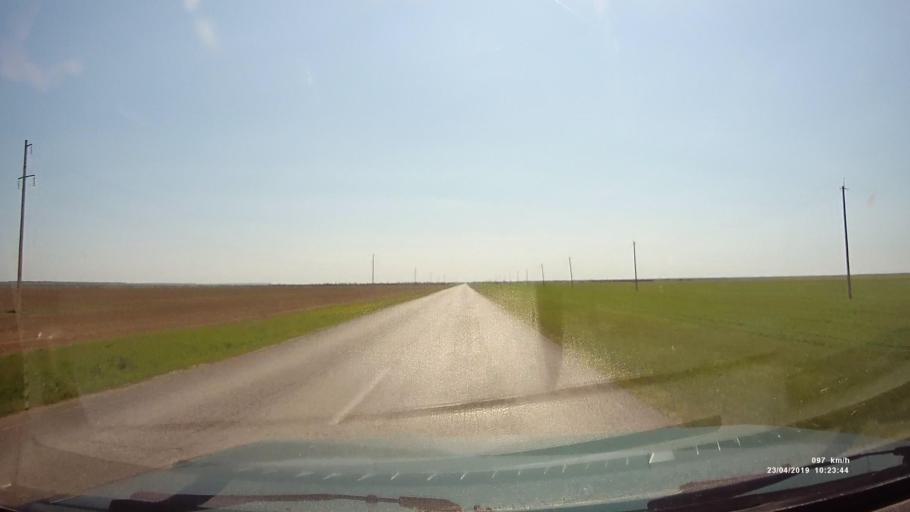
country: RU
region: Rostov
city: Sovetskoye
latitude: 46.6451
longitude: 42.4294
